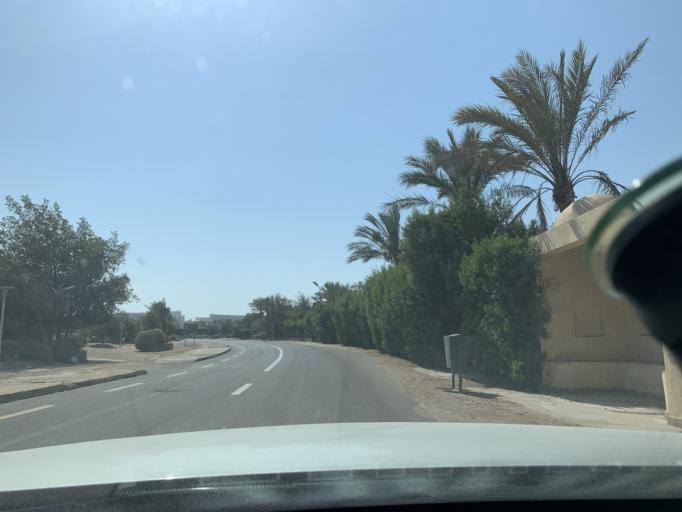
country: EG
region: Red Sea
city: El Gouna
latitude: 27.4035
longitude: 33.6743
